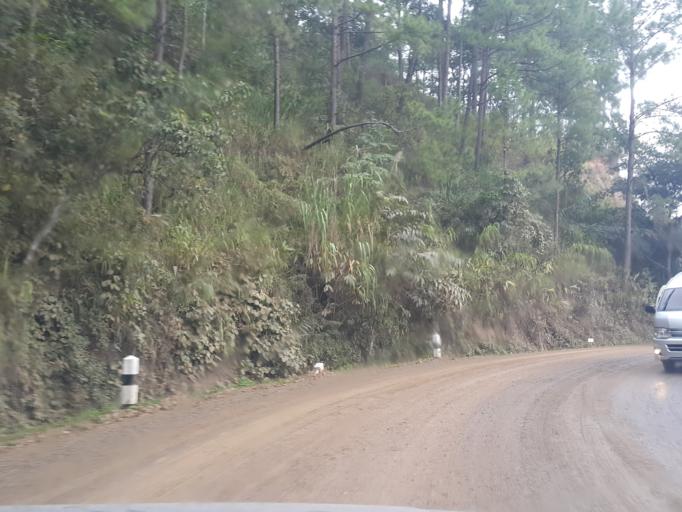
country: TH
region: Mae Hong Son
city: Mae Hi
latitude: 19.2674
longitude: 98.5824
